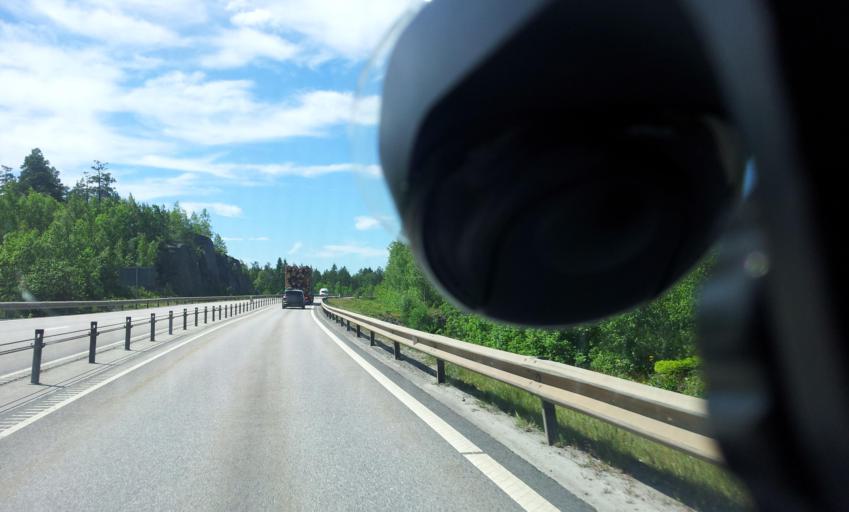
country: SE
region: Kalmar
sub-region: Vasterviks Kommun
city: Vaestervik
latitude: 57.7451
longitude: 16.5568
